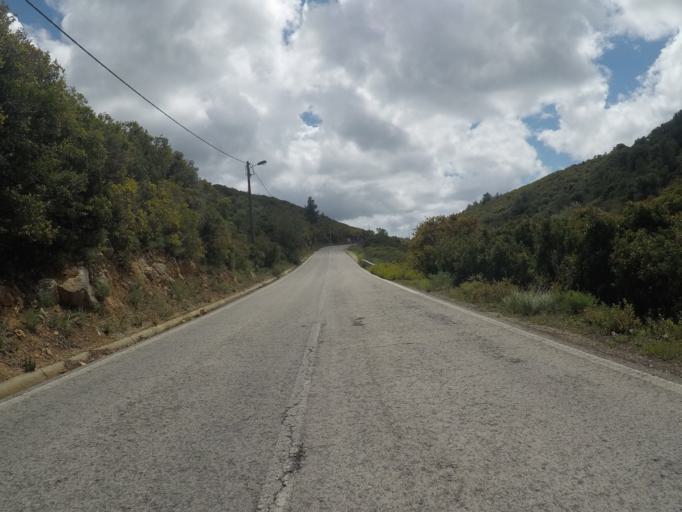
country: PT
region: Faro
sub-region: Vila do Bispo
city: Vila do Bispo
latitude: 37.0713
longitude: -8.8271
